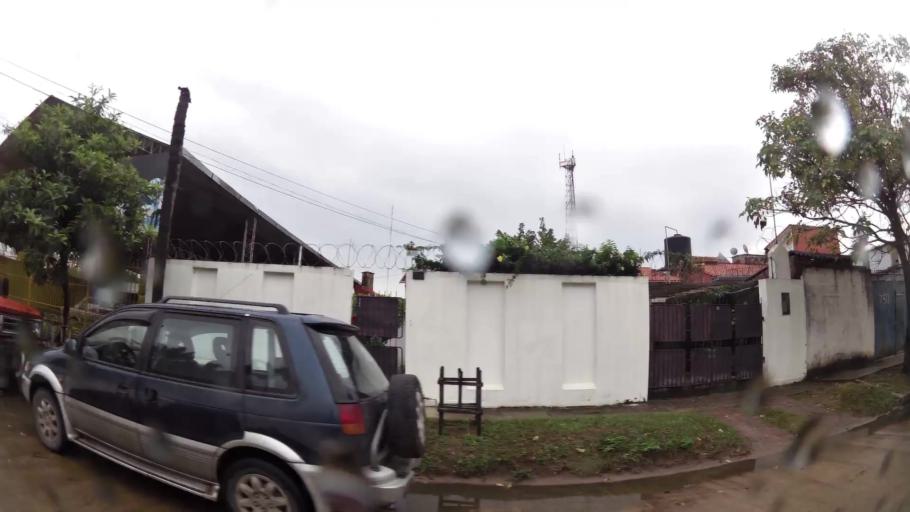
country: BO
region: Santa Cruz
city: Santa Cruz de la Sierra
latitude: -17.8119
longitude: -63.2052
